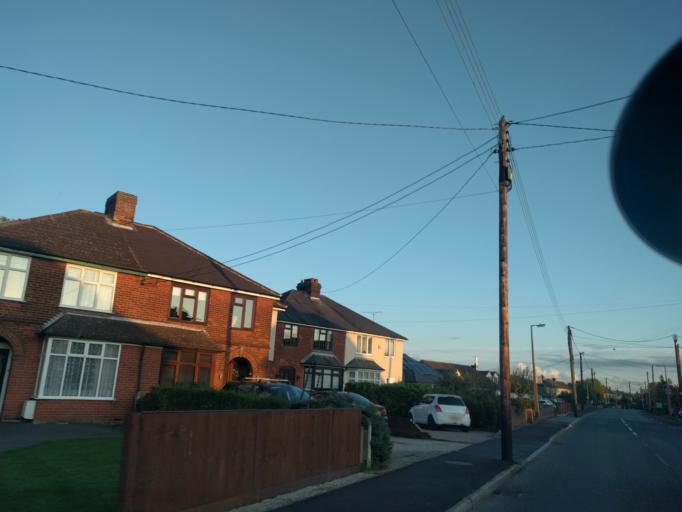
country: GB
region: England
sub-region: Essex
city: Rayne
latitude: 51.8728
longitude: 0.5784
